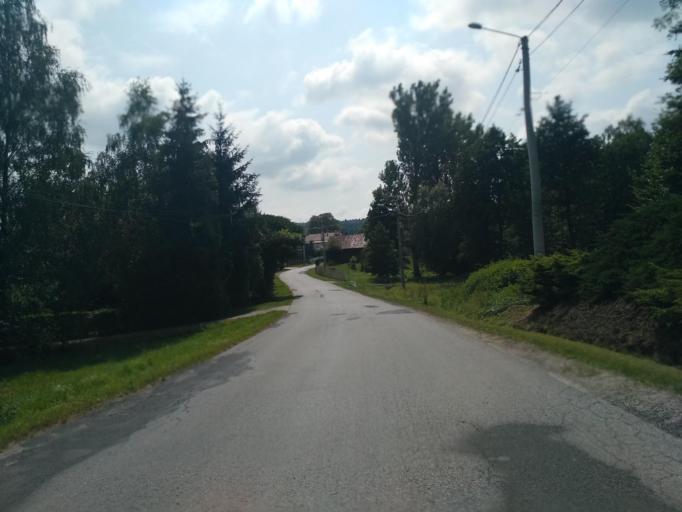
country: PL
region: Subcarpathian Voivodeship
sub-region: Powiat lancucki
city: Kraczkowa
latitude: 50.0217
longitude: 22.1792
